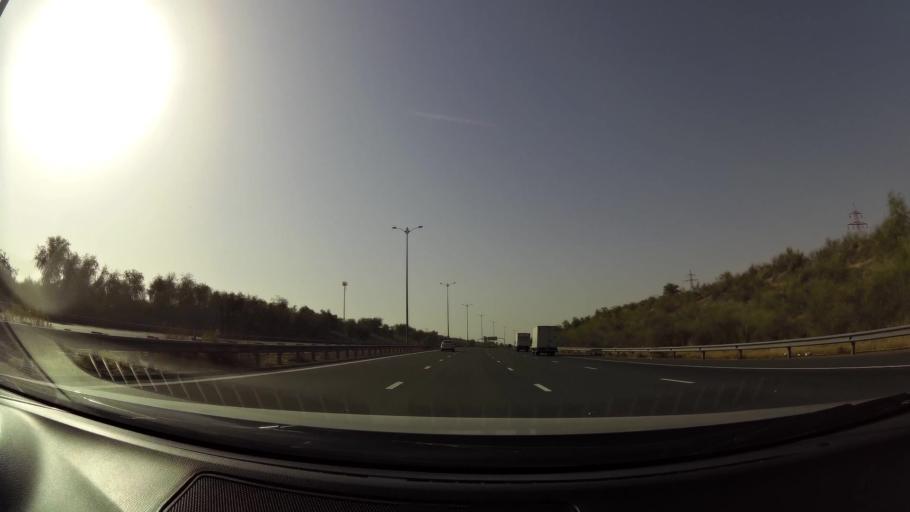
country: OM
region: Al Buraimi
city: Al Buraymi
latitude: 24.6342
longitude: 55.7177
